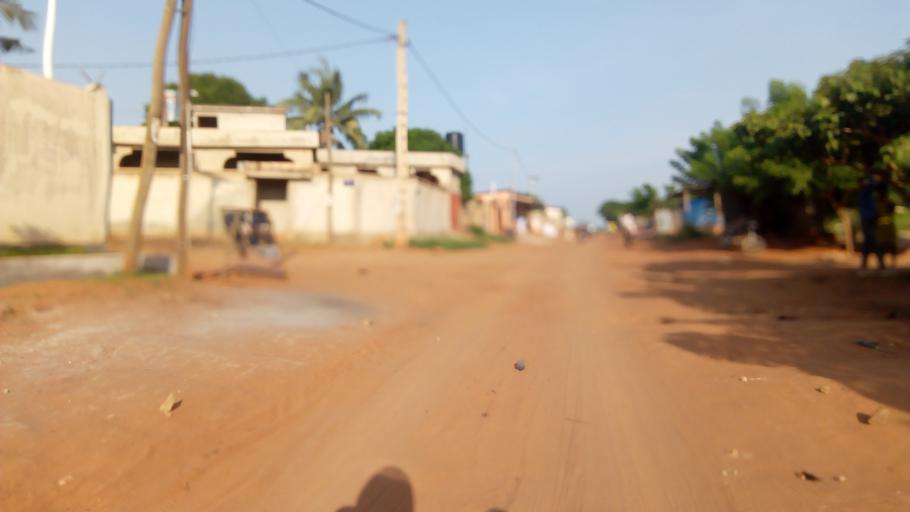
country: TG
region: Maritime
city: Lome
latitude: 6.1777
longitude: 1.1893
